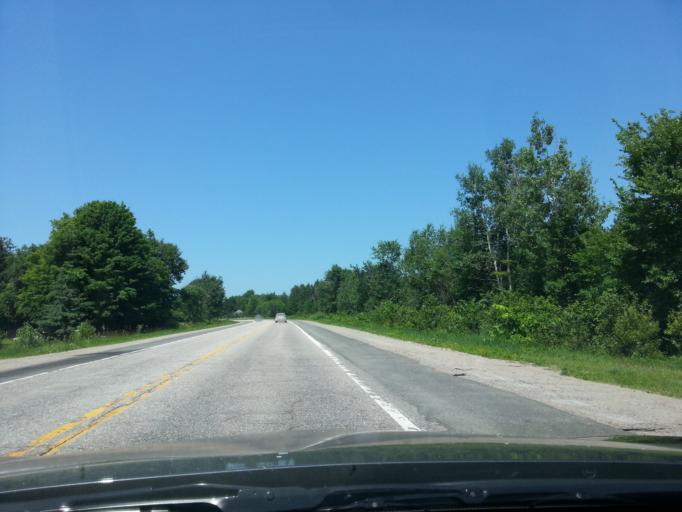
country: CA
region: Ontario
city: Arnprior
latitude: 45.5553
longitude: -76.1247
